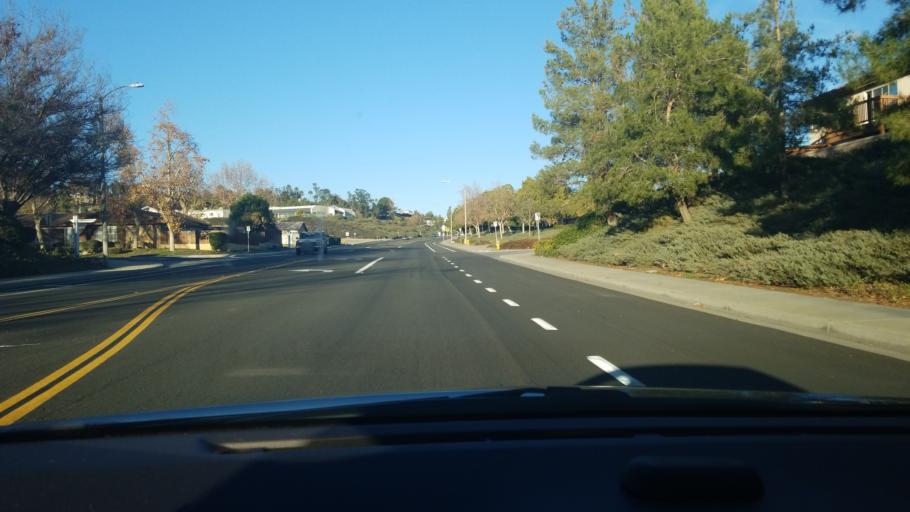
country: US
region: California
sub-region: Riverside County
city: Temecula
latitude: 33.5237
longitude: -117.1146
